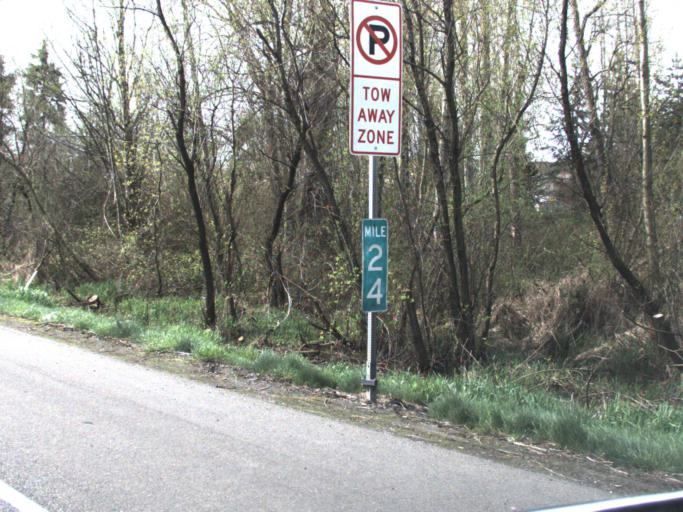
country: US
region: Washington
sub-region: King County
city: Renton
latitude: 47.4353
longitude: -122.2192
